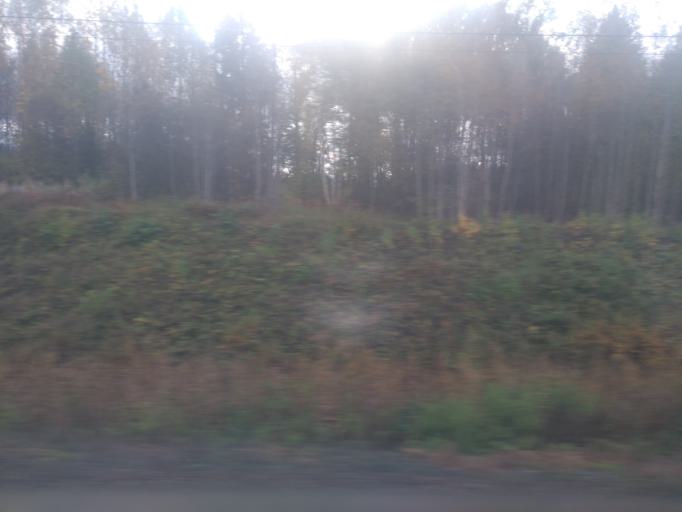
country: RU
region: Udmurtiya
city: Mozhga
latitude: 56.4264
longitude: 52.0566
